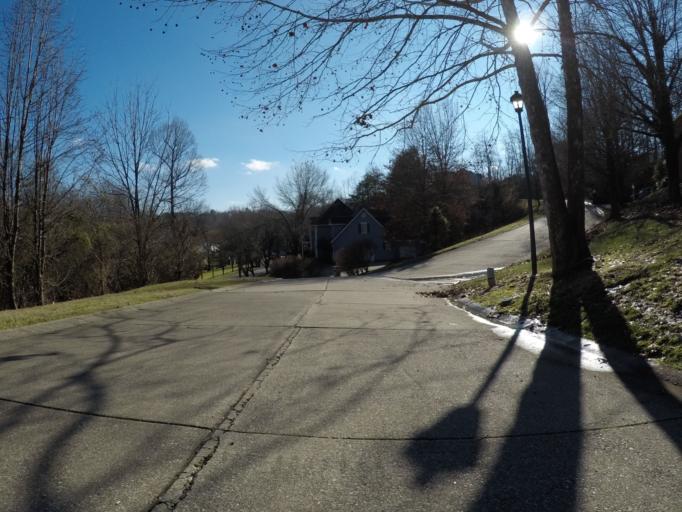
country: US
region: West Virginia
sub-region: Cabell County
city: Pea Ridge
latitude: 38.4156
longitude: -82.3289
